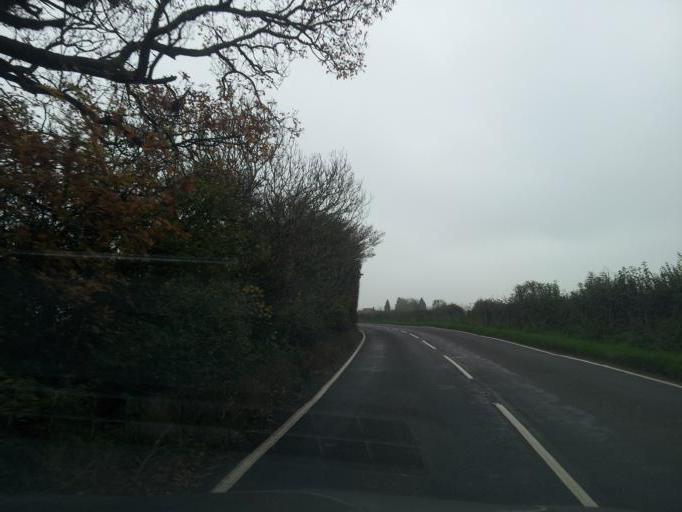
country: GB
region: England
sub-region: Buckinghamshire
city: Buckingham
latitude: 52.0141
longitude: -1.0400
